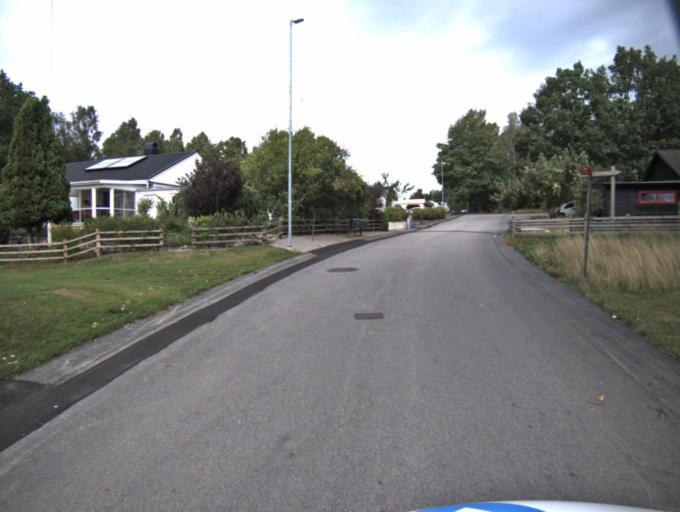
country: SE
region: Vaestra Goetaland
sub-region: Ulricehamns Kommun
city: Ulricehamn
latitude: 57.8447
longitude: 13.2725
